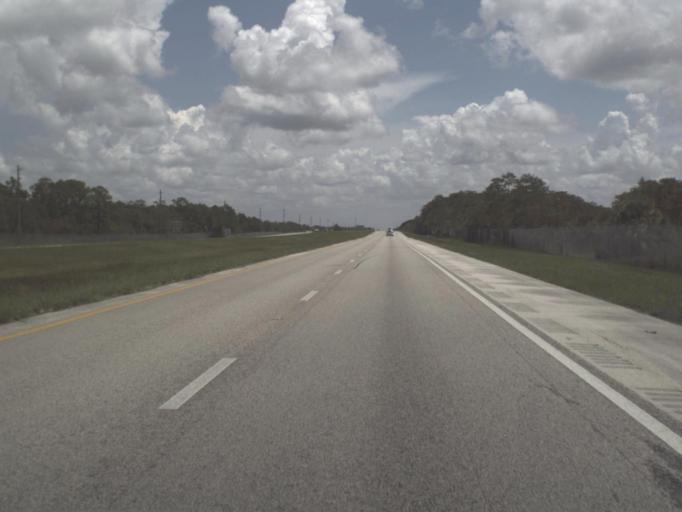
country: US
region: Florida
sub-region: Collier County
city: Immokalee
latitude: 26.1687
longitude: -81.0567
